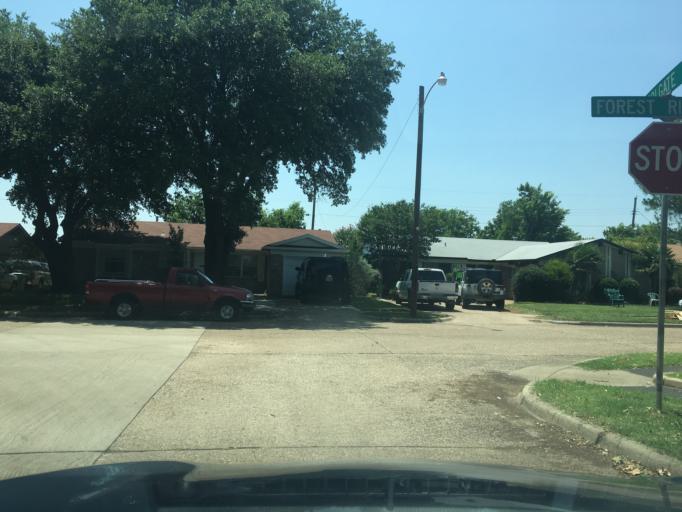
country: US
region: Texas
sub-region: Dallas County
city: Richardson
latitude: 32.9192
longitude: -96.7050
